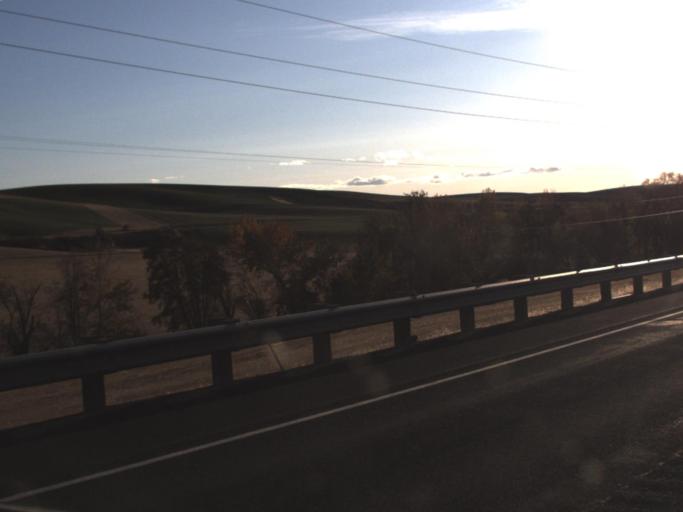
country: US
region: Washington
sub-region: Walla Walla County
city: Waitsburg
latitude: 46.1312
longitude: -118.1822
